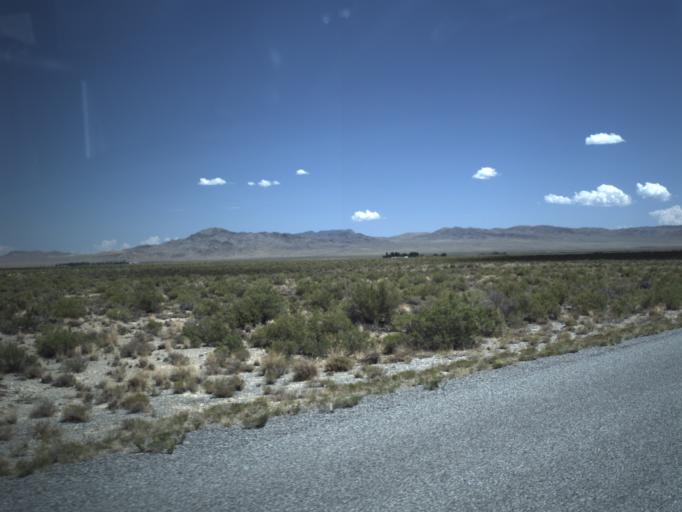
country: US
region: Nevada
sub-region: White Pine County
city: McGill
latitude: 39.0544
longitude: -114.0132
